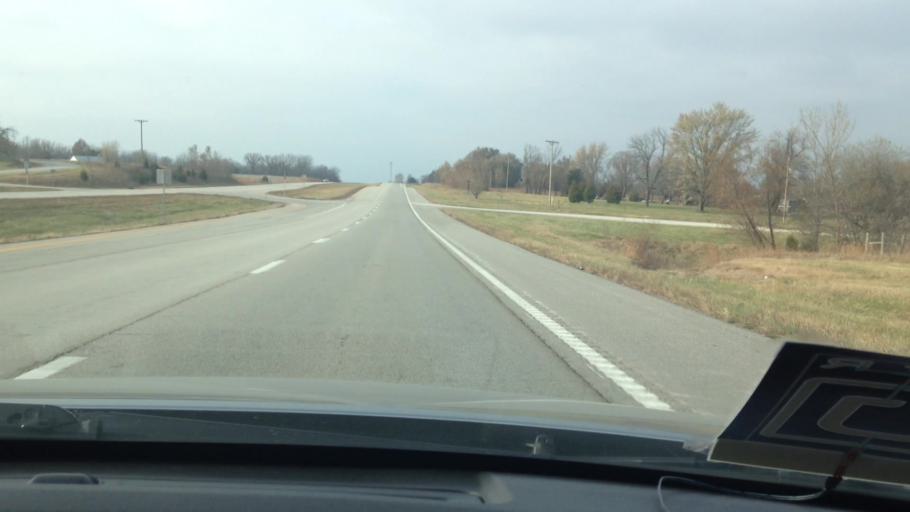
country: US
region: Missouri
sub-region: Cass County
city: Garden City
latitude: 38.5394
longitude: -94.1604
